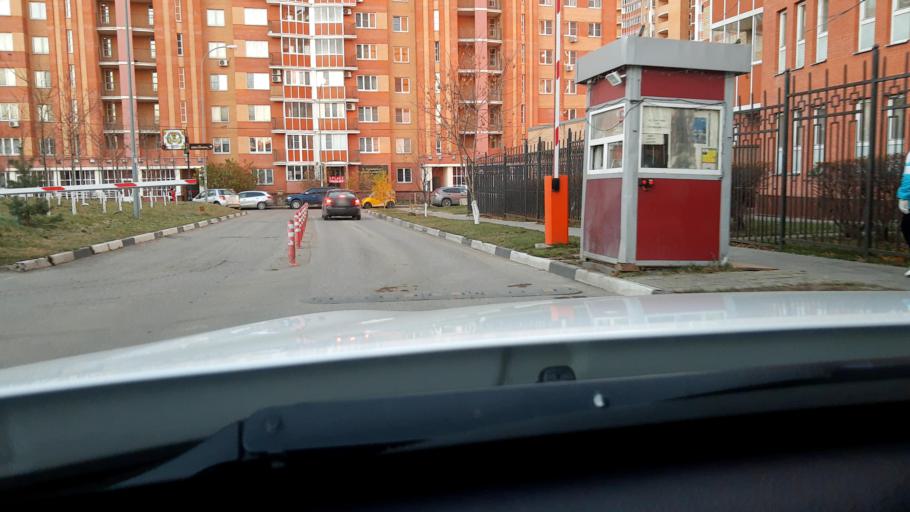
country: RU
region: Moskovskaya
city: Lesnoy Gorodok
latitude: 55.6600
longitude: 37.2297
